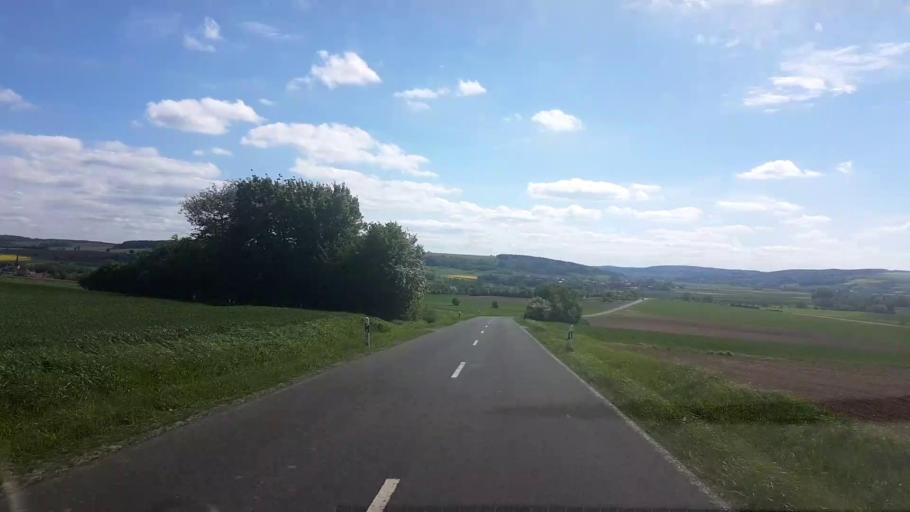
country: DE
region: Bavaria
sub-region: Regierungsbezirk Unterfranken
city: Untermerzbach
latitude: 50.1462
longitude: 10.8902
